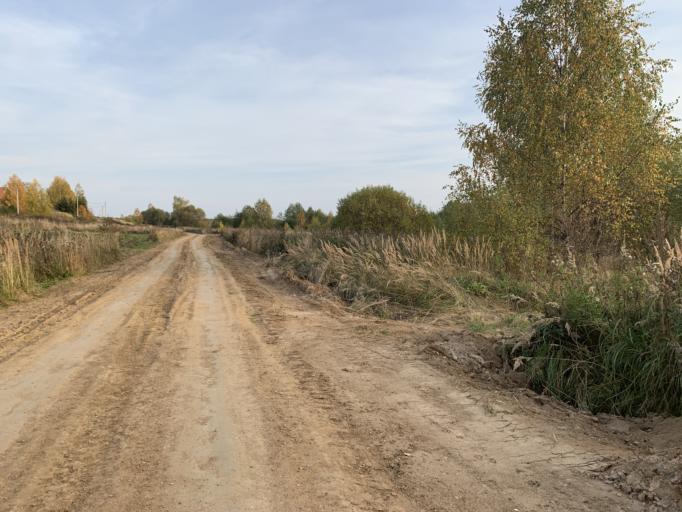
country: RU
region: Jaroslavl
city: Petrovsk
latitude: 56.9800
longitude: 39.3772
